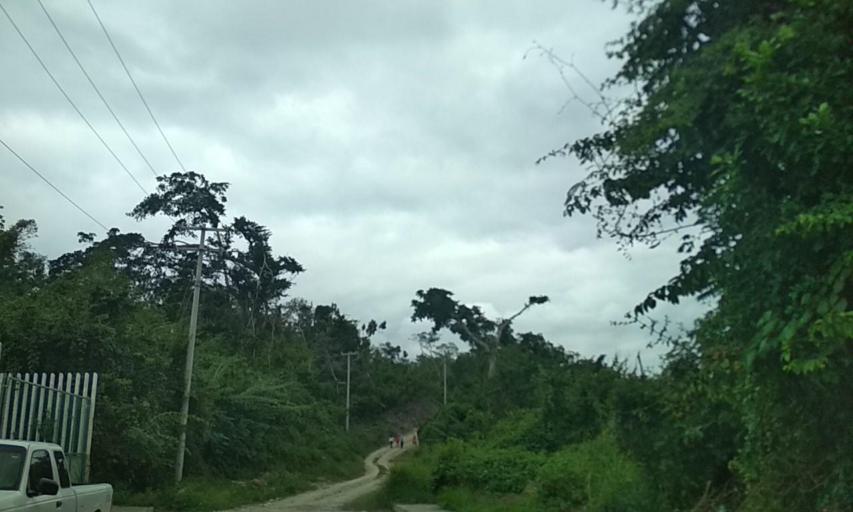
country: MX
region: Veracruz
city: Papantla de Olarte
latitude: 20.4743
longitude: -97.3206
